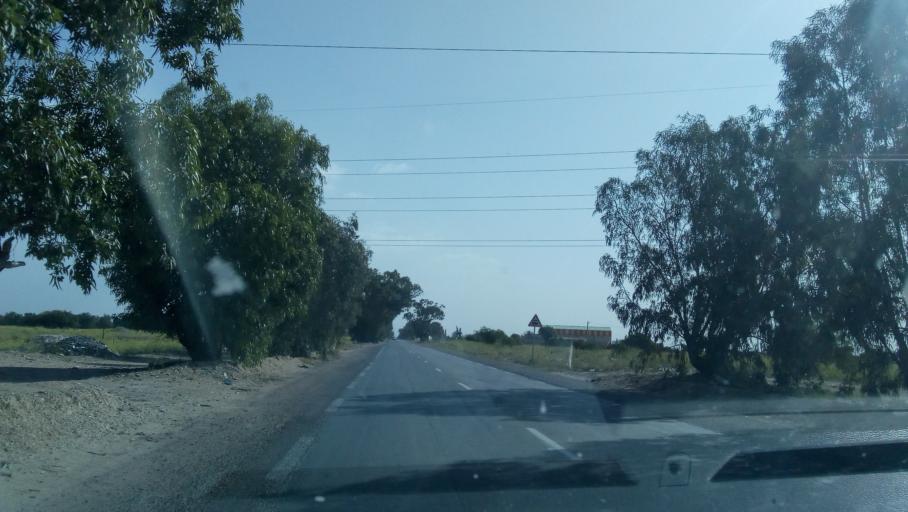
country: TN
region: Qabis
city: Gabes
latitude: 33.8920
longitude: 10.0362
